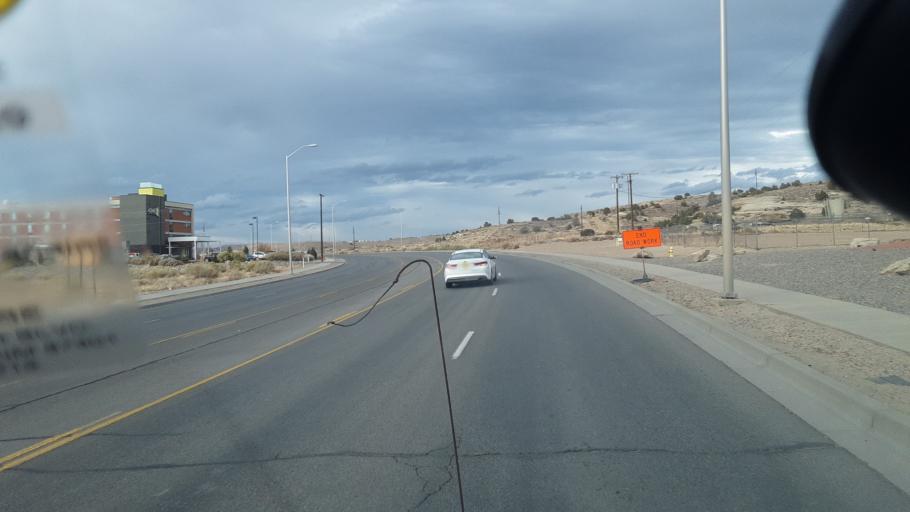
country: US
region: New Mexico
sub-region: San Juan County
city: Farmington
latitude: 36.7217
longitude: -108.1577
